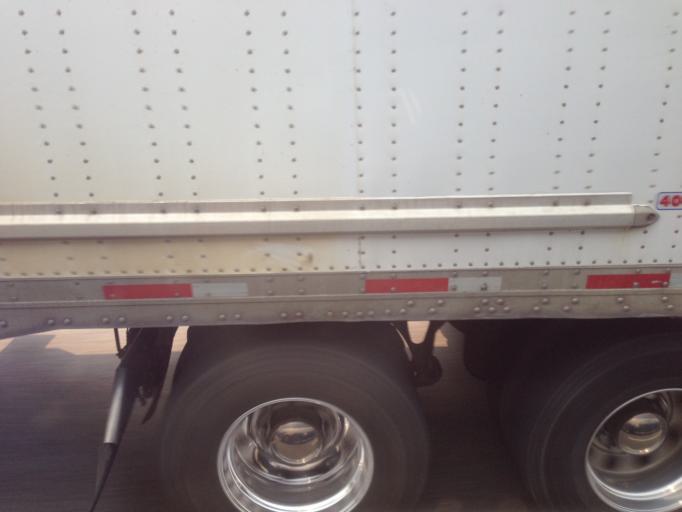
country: CA
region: Alberta
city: Canmore
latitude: 51.1426
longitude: -115.4172
